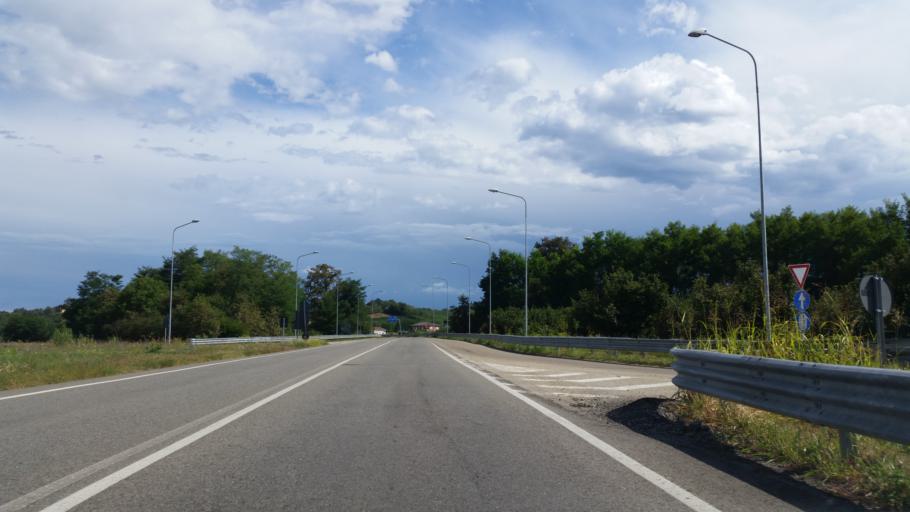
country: IT
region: Piedmont
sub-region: Provincia di Cuneo
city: Monta
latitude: 44.8163
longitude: 7.9471
